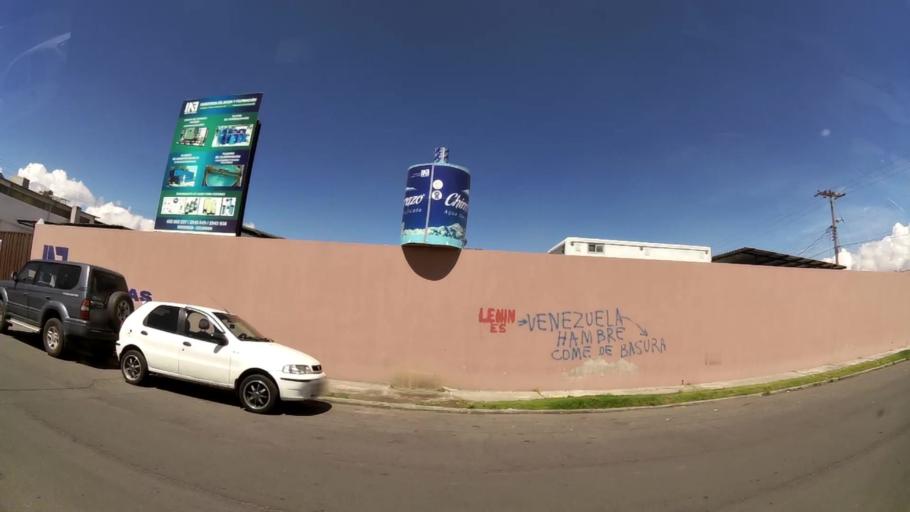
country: EC
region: Chimborazo
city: Riobamba
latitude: -1.6767
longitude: -78.6318
